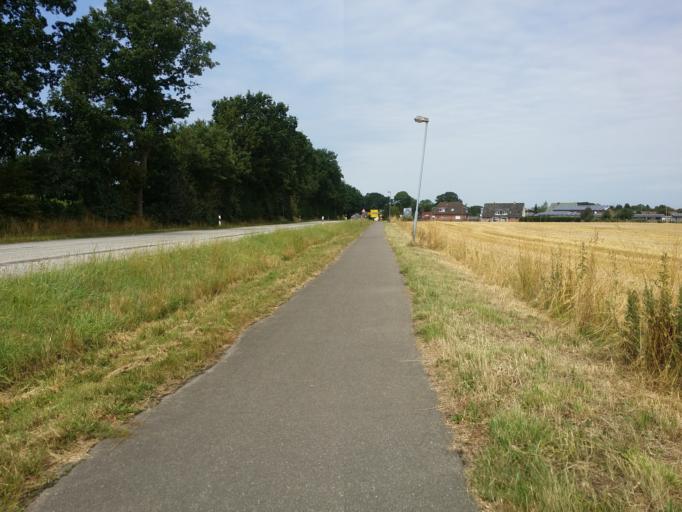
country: DE
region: Schleswig-Holstein
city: Vaale
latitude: 53.9954
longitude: 9.3836
